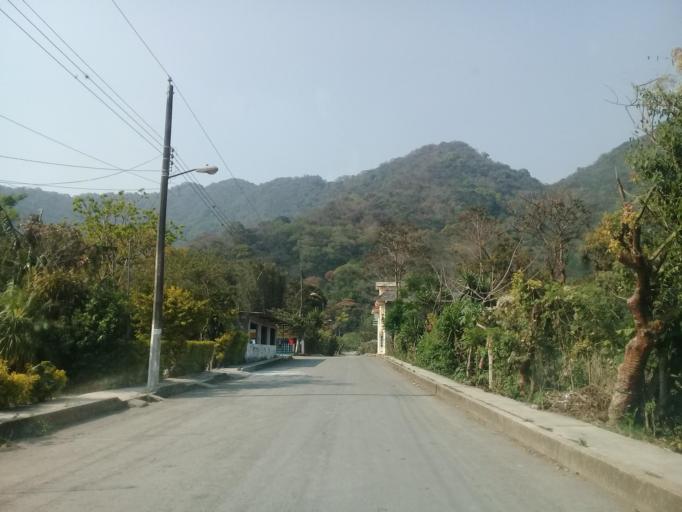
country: MX
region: Veracruz
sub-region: Ixtaczoquitlan
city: Campo Chico
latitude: 18.8363
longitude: -97.0260
